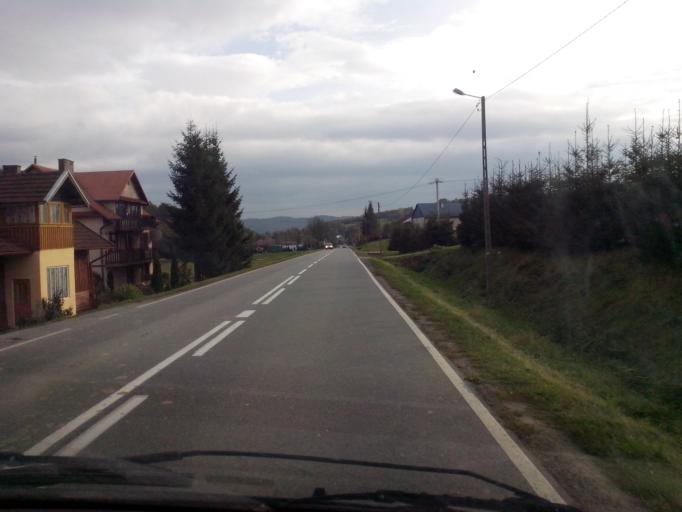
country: PL
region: Subcarpathian Voivodeship
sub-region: Powiat strzyzowski
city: Wisniowa
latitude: 49.8950
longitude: 21.6432
